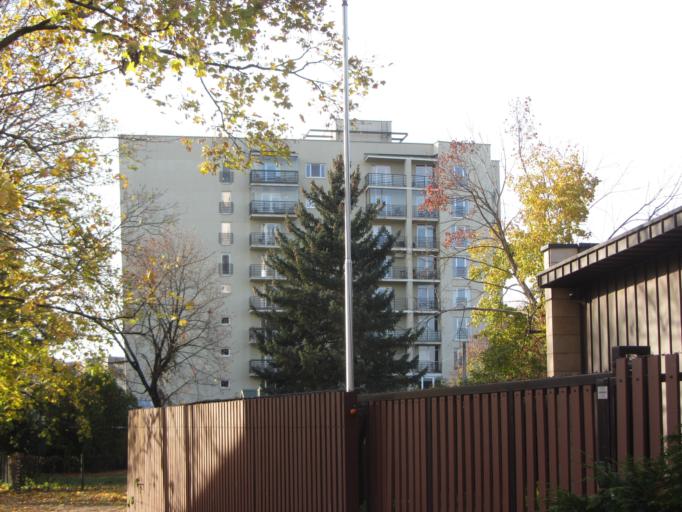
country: LT
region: Vilnius County
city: Vilkpede
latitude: 54.6789
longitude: 25.2536
